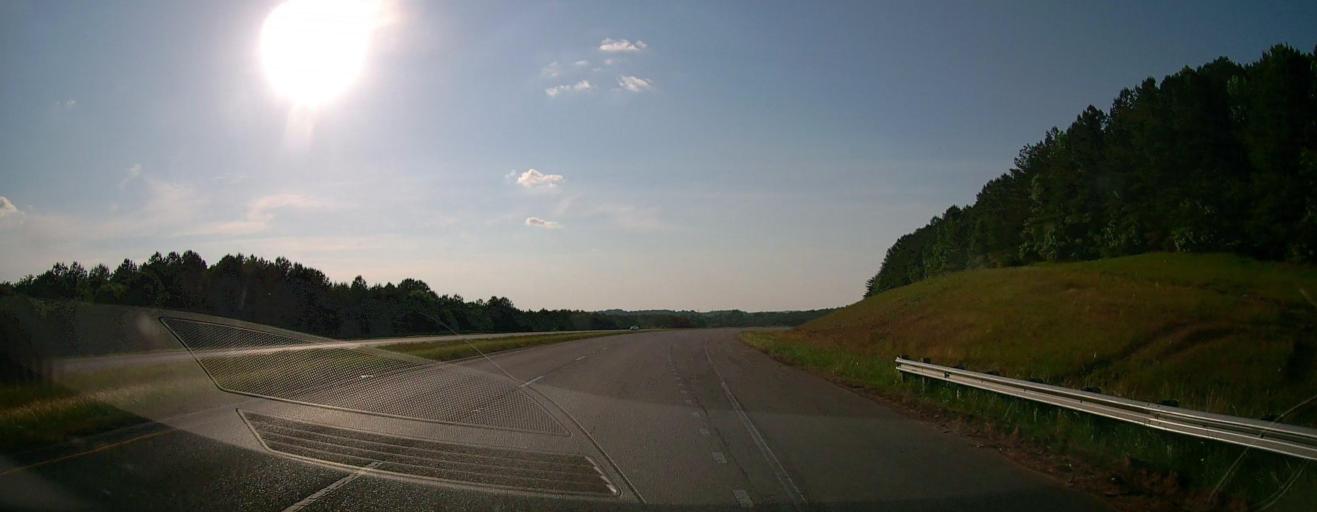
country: US
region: Alabama
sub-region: Walker County
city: Jasper
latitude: 33.8139
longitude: -87.3079
